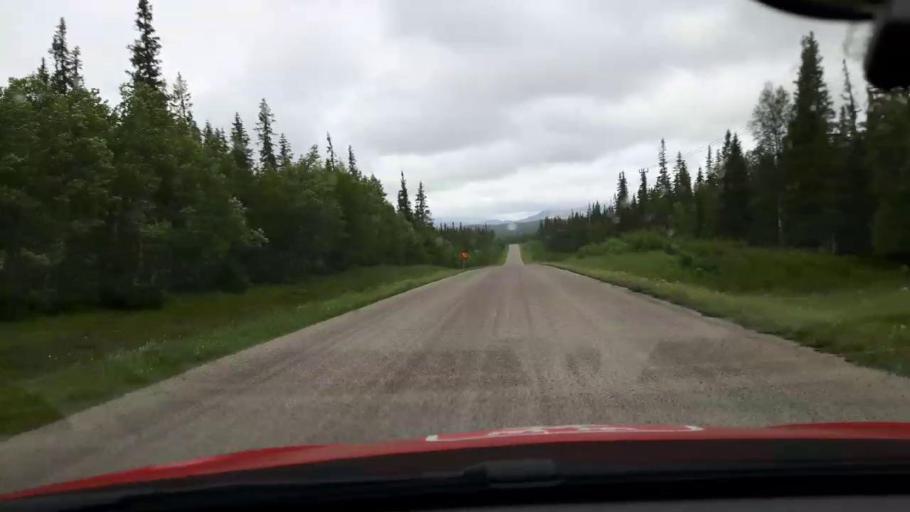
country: NO
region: Nord-Trondelag
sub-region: Meraker
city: Meraker
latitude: 63.2762
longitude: 12.3595
